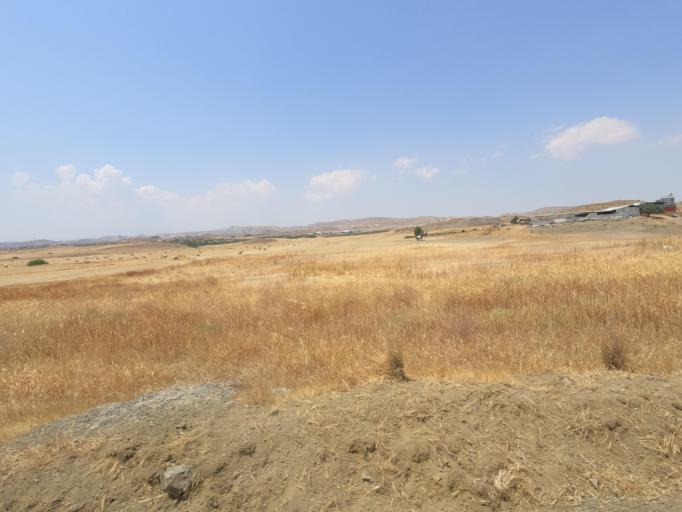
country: CY
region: Larnaka
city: Troulloi
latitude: 35.0168
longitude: 33.6043
